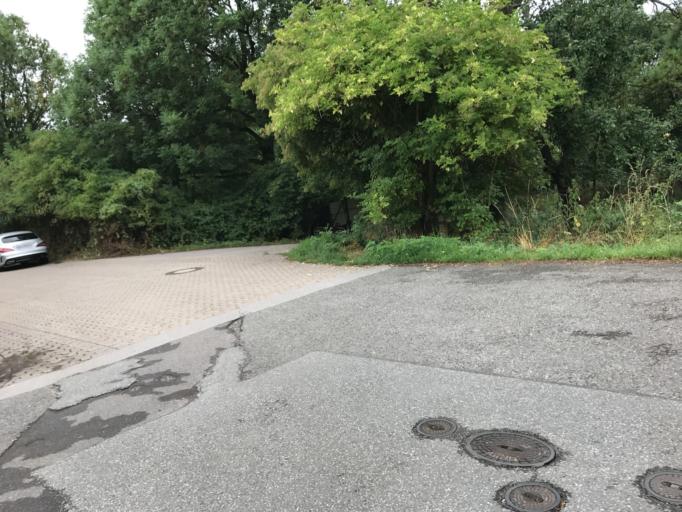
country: DE
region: North Rhine-Westphalia
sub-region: Regierungsbezirk Dusseldorf
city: Hochfeld
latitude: 51.3611
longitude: 6.6835
